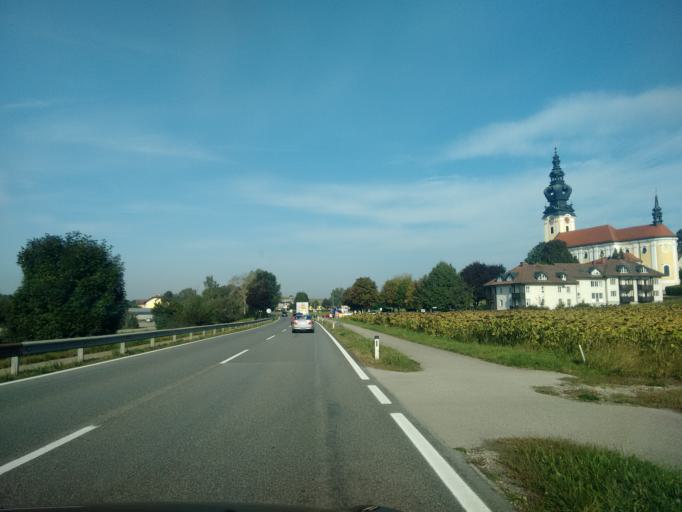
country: AT
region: Upper Austria
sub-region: Politischer Bezirk Grieskirchen
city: Grieskirchen
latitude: 48.2797
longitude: 13.7154
